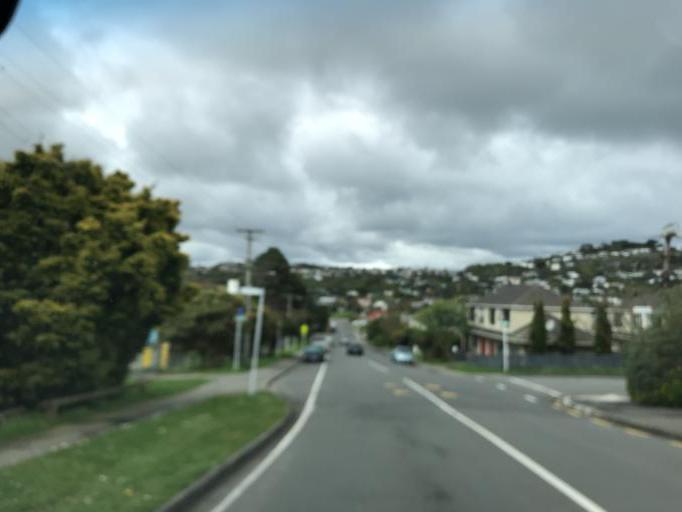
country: NZ
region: Wellington
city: Petone
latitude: -41.2198
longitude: 174.8037
